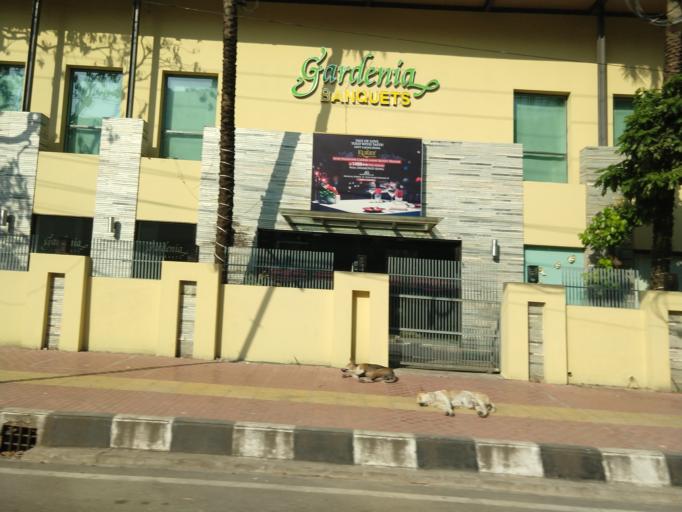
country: BD
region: Dhaka
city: Paltan
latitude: 23.7960
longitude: 90.4120
